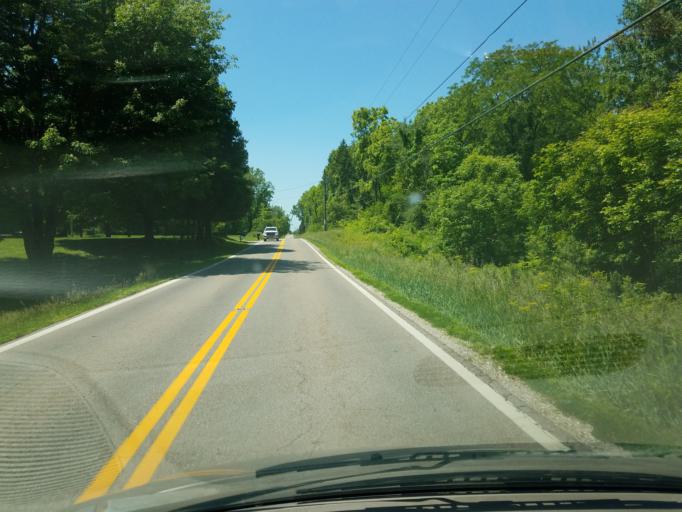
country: US
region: Ohio
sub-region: Knox County
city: Centerburg
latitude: 40.3363
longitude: -82.8000
